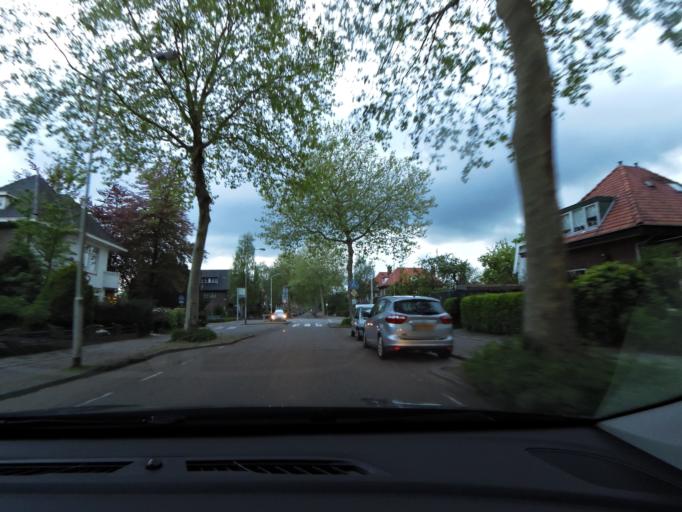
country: NL
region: South Holland
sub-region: Gemeente Gorinchem
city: Gorinchem
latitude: 51.8368
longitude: 4.9704
